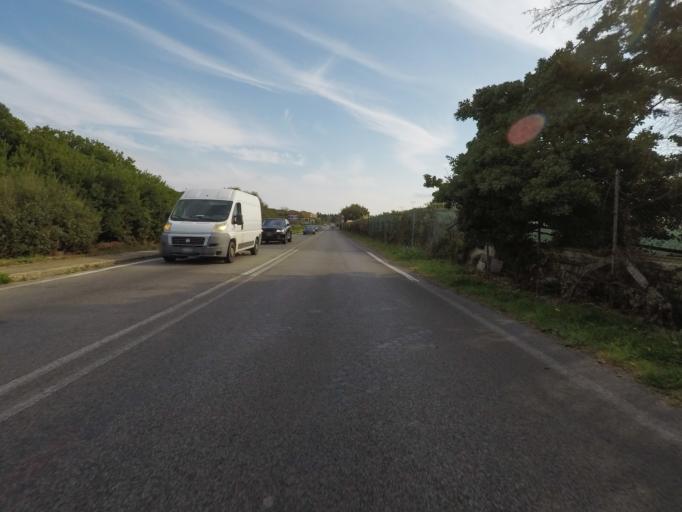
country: IT
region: Latium
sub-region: Citta metropolitana di Roma Capitale
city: Civitavecchia
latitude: 42.0636
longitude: 11.8145
